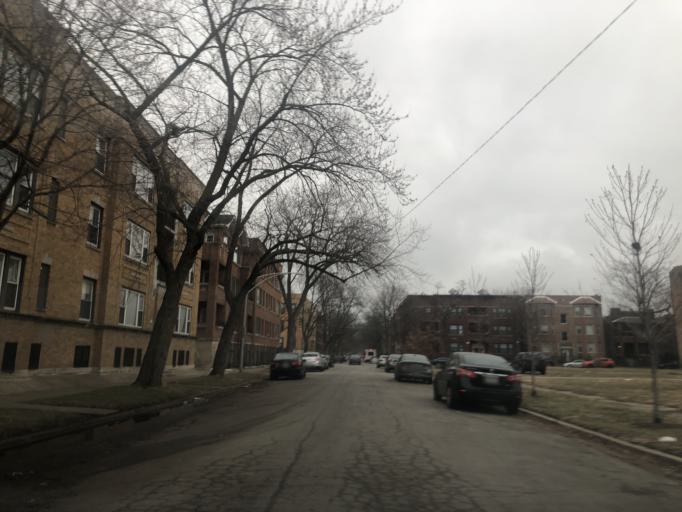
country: US
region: Illinois
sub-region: Cook County
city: Chicago
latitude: 41.7821
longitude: -87.6145
